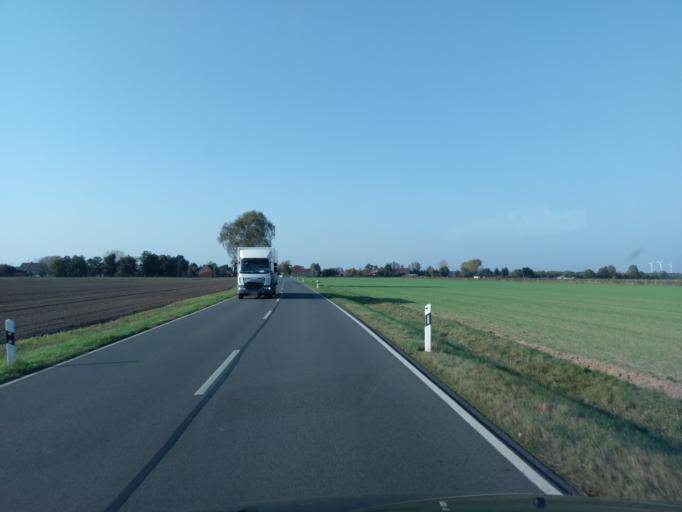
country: DE
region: Brandenburg
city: Falkenberg
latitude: 51.5365
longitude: 13.2880
